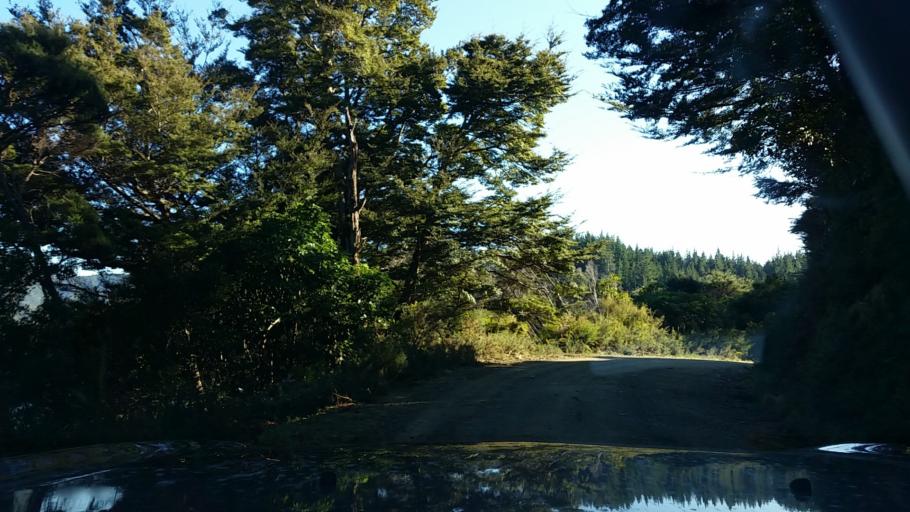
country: NZ
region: Marlborough
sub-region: Marlborough District
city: Picton
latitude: -41.1251
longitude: 173.9913
